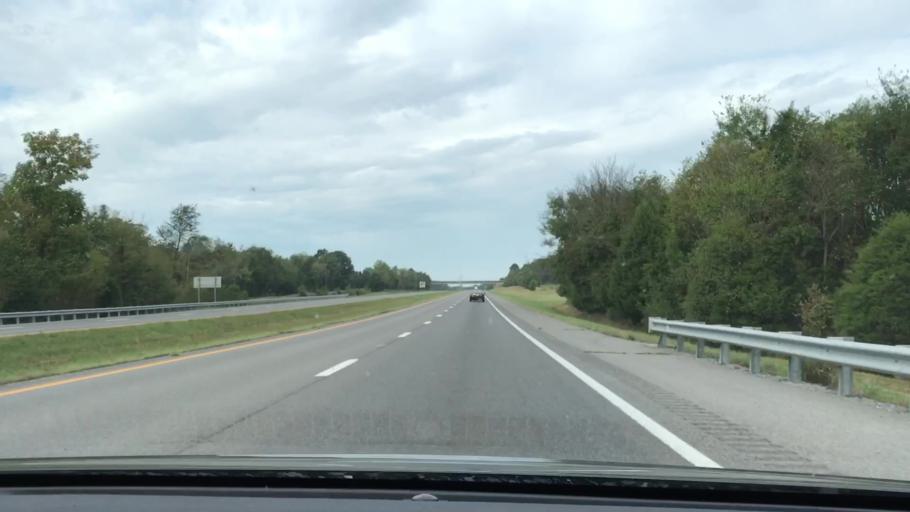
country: US
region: Kentucky
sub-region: Graves County
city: Mayfield
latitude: 36.7788
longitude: -88.5752
